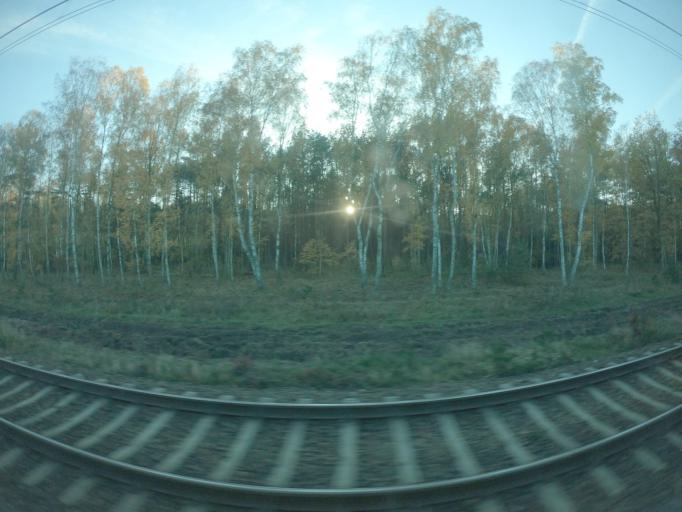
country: PL
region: Lubusz
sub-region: Powiat slubicki
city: Rzepin
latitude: 52.2837
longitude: 14.8997
